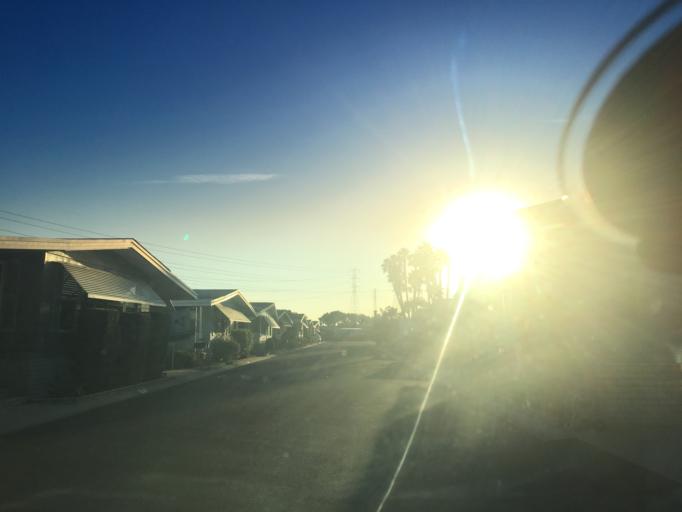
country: US
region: California
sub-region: Orange County
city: Orange
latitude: 33.8139
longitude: -117.8797
